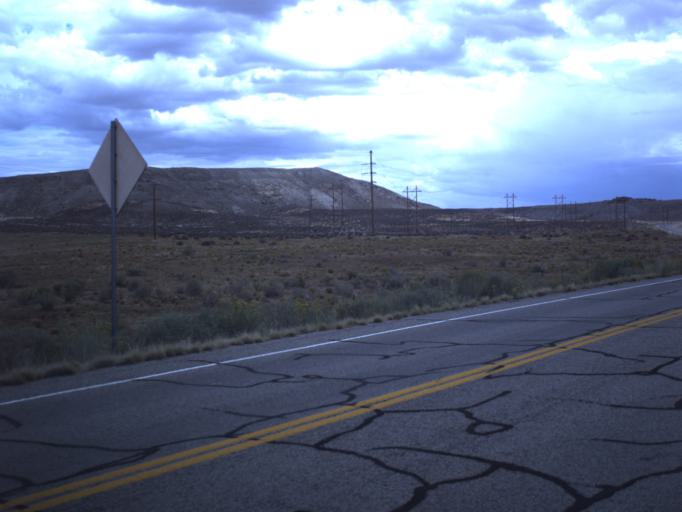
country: US
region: Utah
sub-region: San Juan County
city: Blanding
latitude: 37.2800
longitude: -109.3736
